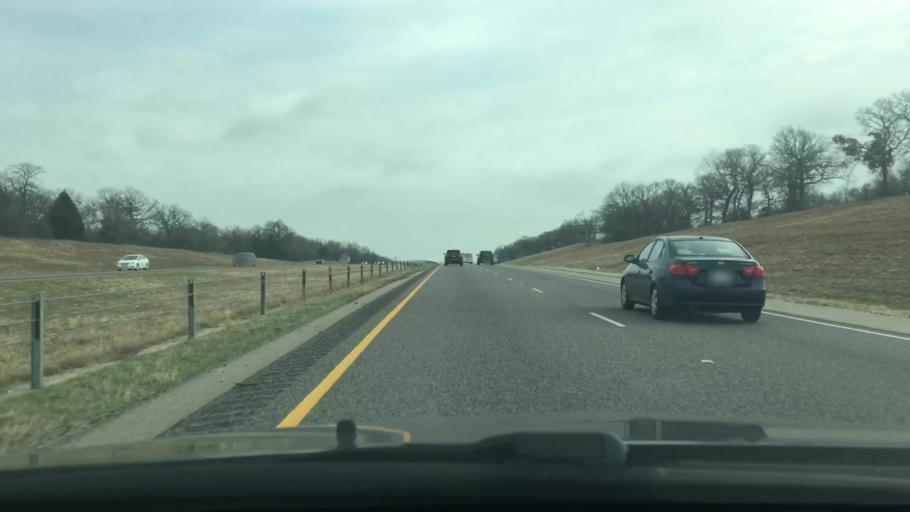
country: US
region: Texas
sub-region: Leon County
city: Buffalo
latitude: 31.5325
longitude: -96.1178
